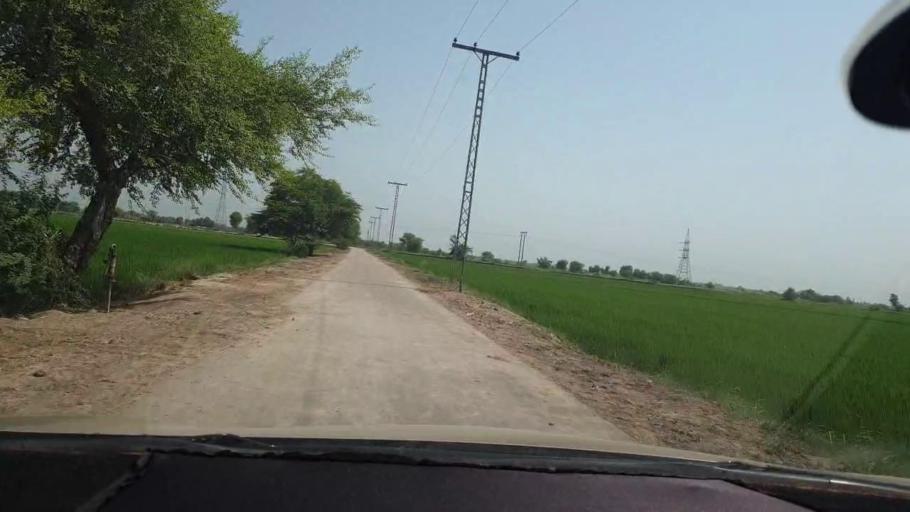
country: PK
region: Sindh
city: Kambar
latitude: 27.5009
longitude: 68.0169
